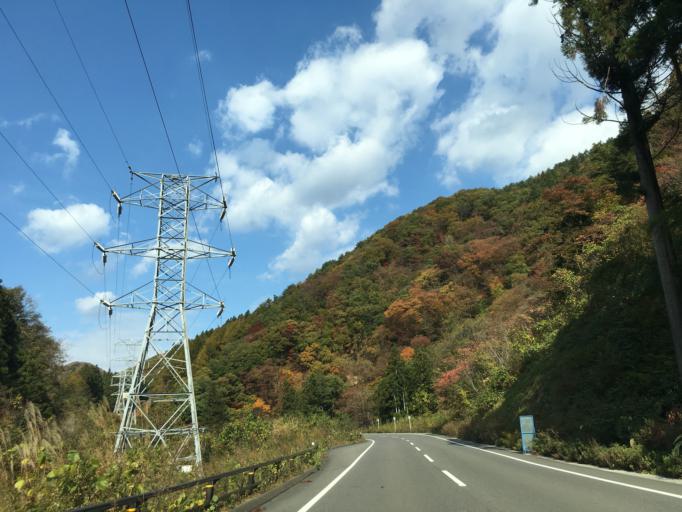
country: JP
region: Fukushima
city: Sukagawa
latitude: 37.3088
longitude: 140.1444
